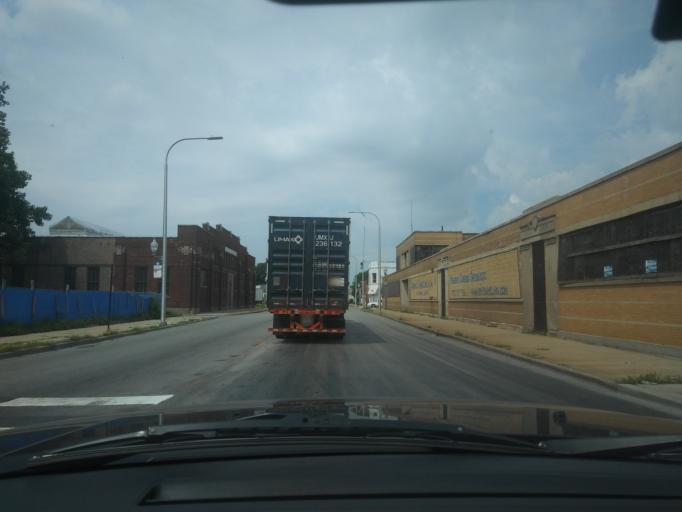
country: US
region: Illinois
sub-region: Cook County
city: Chicago
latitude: 41.7871
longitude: -87.6604
